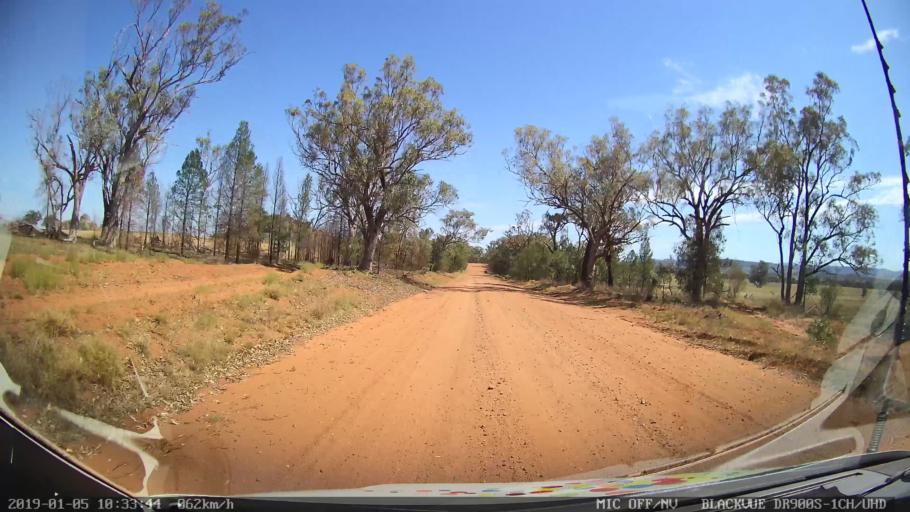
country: AU
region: New South Wales
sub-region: Gilgandra
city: Gilgandra
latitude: -31.5045
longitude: 148.9297
